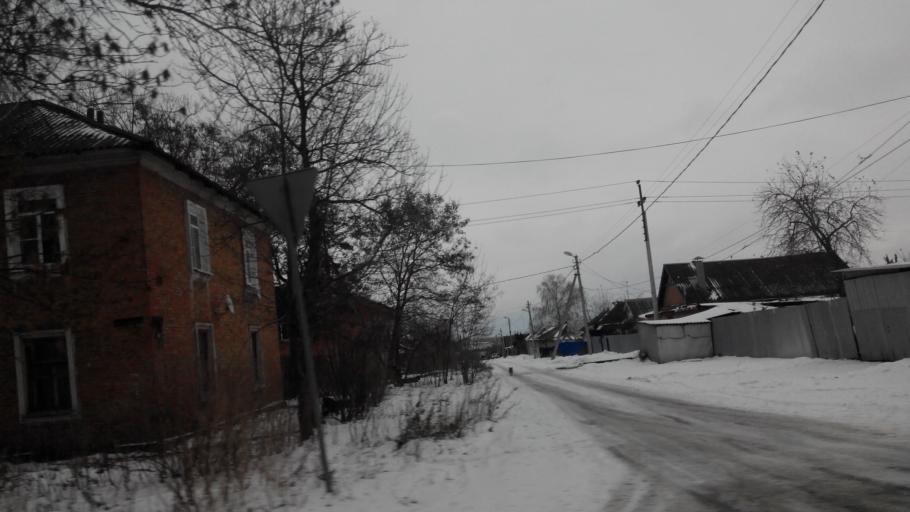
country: RU
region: Tula
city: Uzlovaya
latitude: 53.9827
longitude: 38.1911
